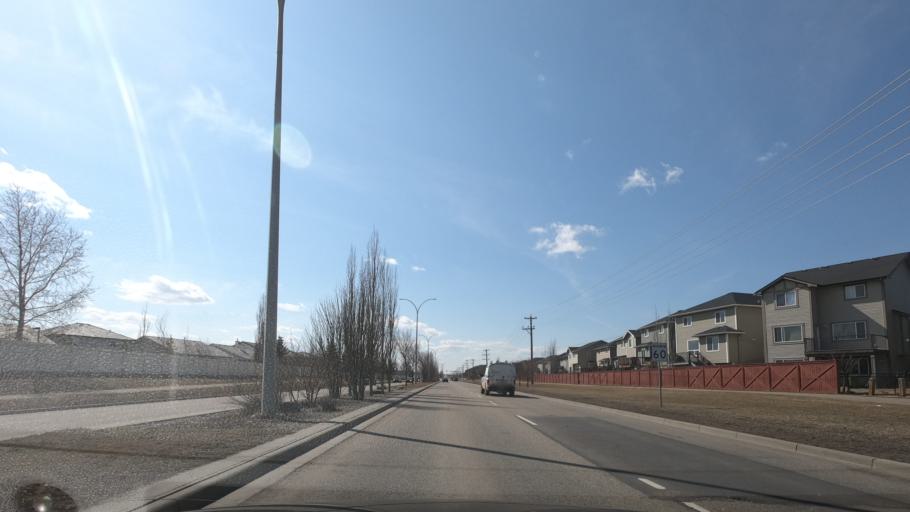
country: CA
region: Alberta
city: Airdrie
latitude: 51.3001
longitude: -114.0283
